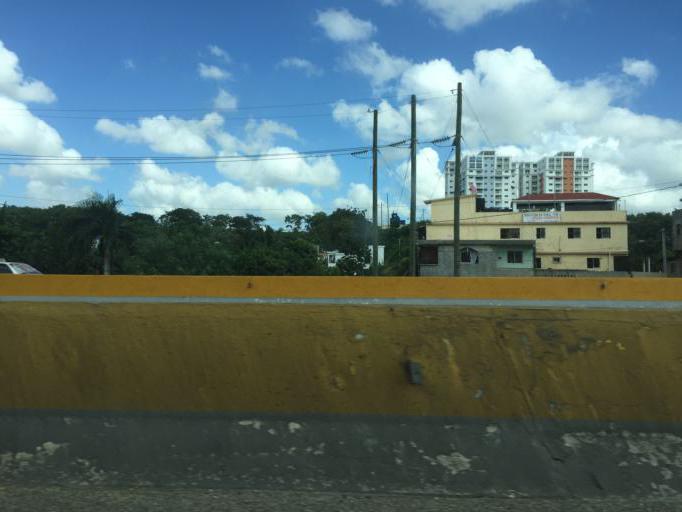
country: DO
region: Santo Domingo
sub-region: Santo Domingo
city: Santo Domingo Este
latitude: 18.4819
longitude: -69.8436
